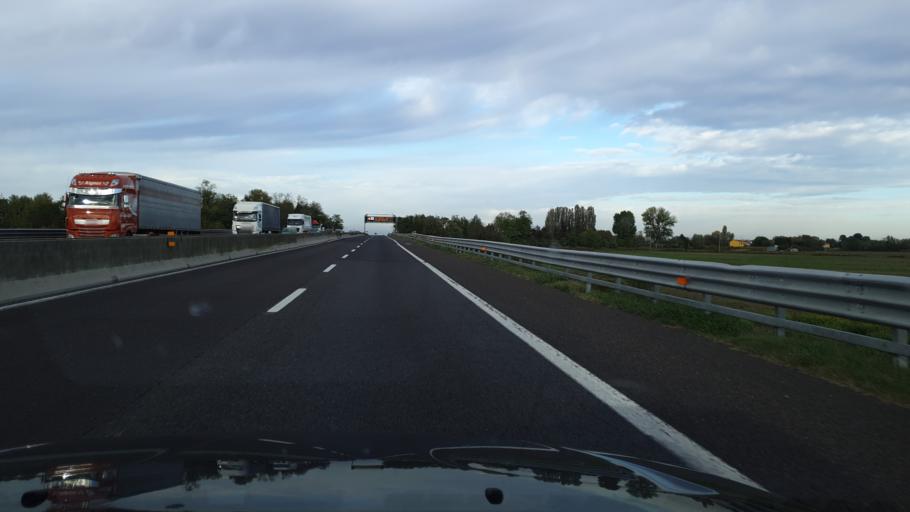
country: IT
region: Veneto
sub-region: Provincia di Rovigo
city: Grignano Polesine
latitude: 45.0685
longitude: 11.7312
